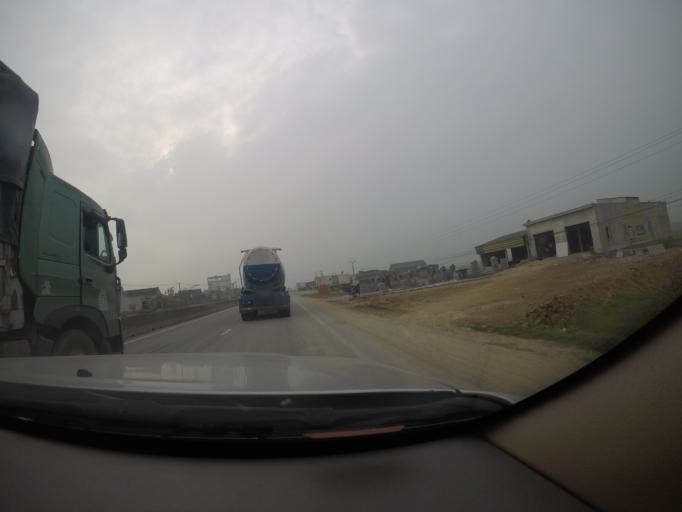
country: VN
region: Ha Tinh
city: Ky Anh
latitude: 18.1888
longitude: 106.1874
